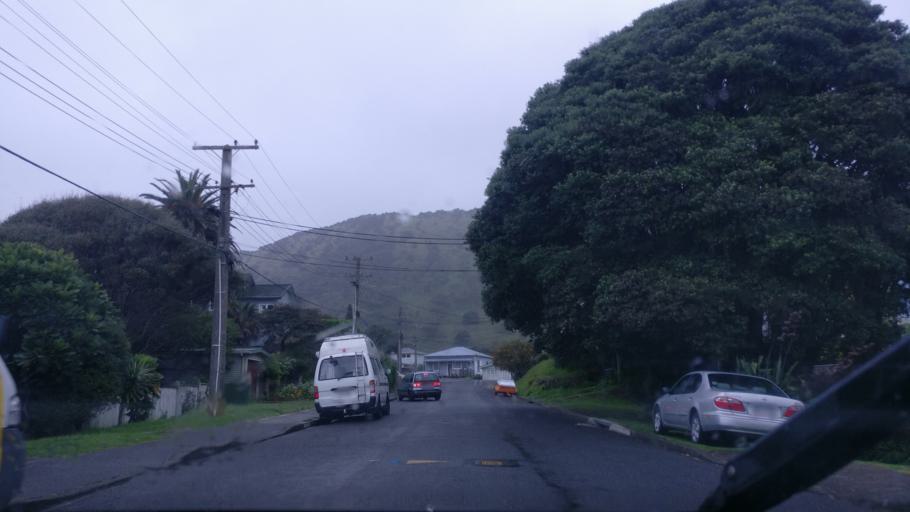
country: NZ
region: Wellington
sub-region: Kapiti Coast District
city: Paraparaumu
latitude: -40.9831
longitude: 174.9570
